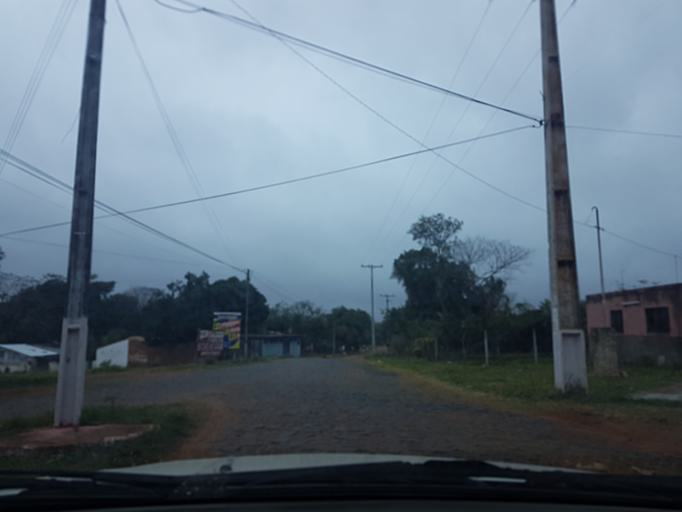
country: PY
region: Central
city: San Lorenzo
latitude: -25.2763
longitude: -57.4618
